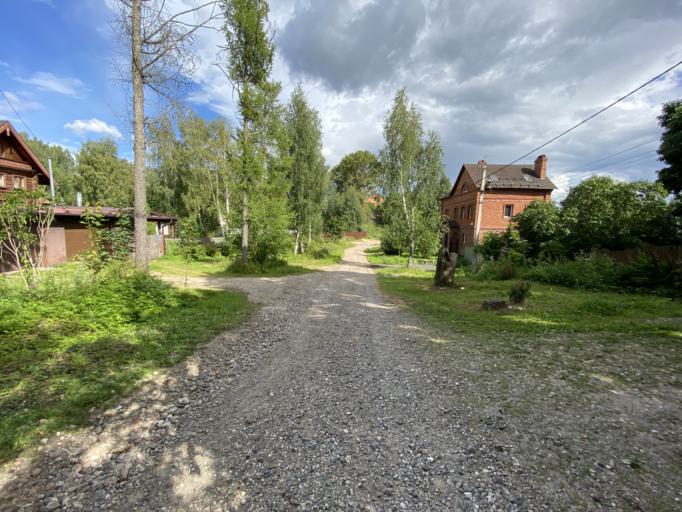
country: RU
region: Moskovskaya
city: Sergiyev Posad
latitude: 56.3084
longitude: 38.1562
